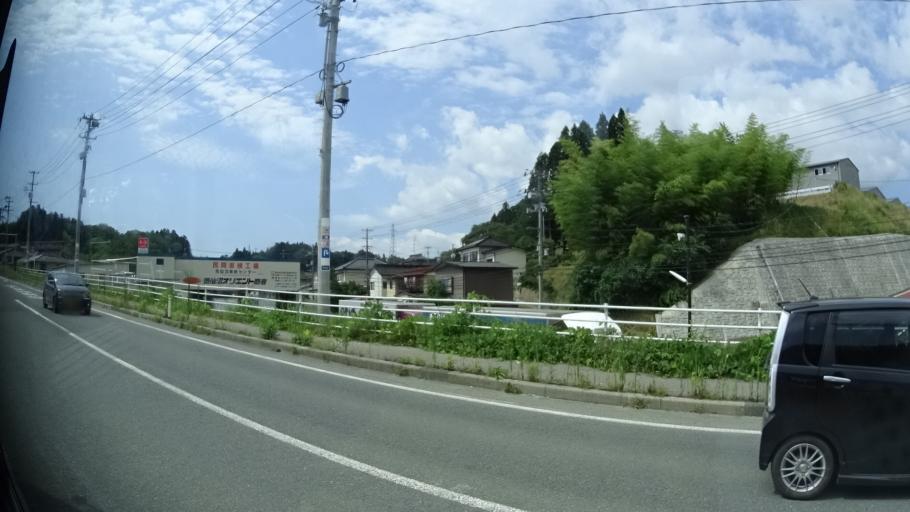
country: JP
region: Iwate
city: Ofunato
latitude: 38.8881
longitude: 141.5713
